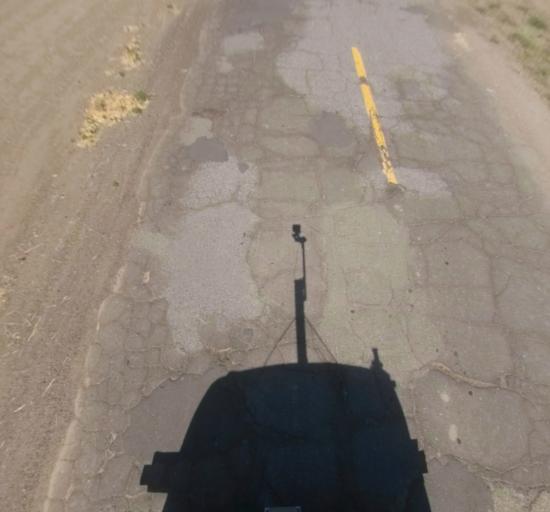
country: US
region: California
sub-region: Madera County
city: Chowchilla
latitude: 37.0327
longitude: -120.3222
